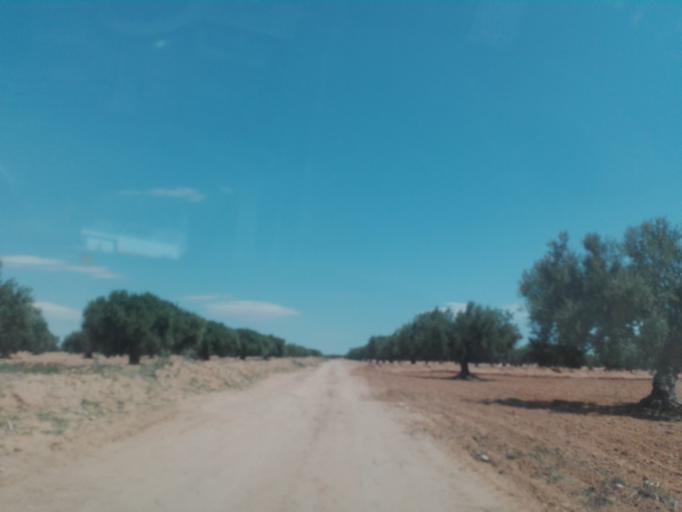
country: TN
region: Safaqis
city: Sfax
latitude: 34.6584
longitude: 10.5998
